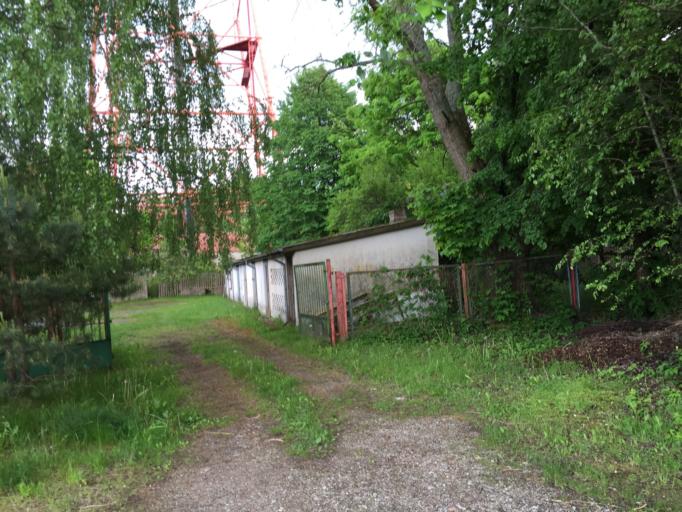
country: LT
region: Klaipedos apskritis
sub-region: Klaipeda
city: Klaipeda
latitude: 55.7683
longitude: 21.0959
